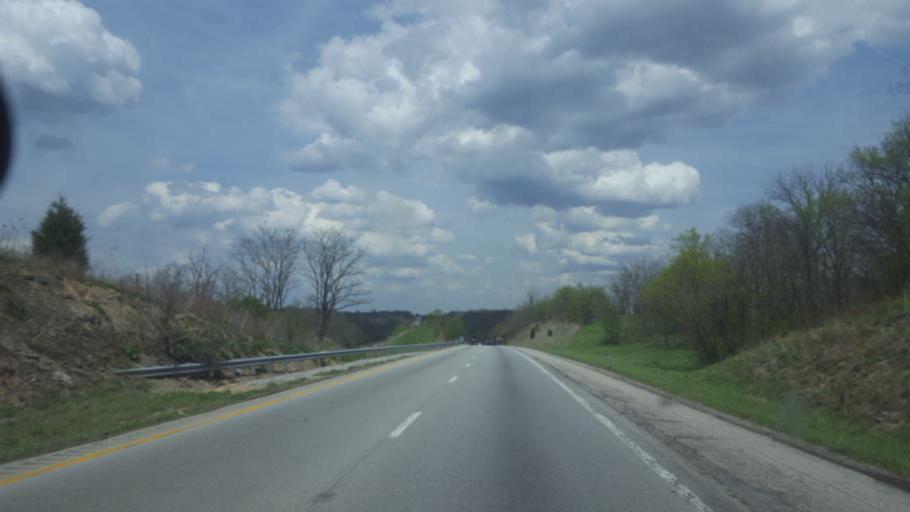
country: US
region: Kentucky
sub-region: Trimble County
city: Providence
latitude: 38.5029
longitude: -85.2465
